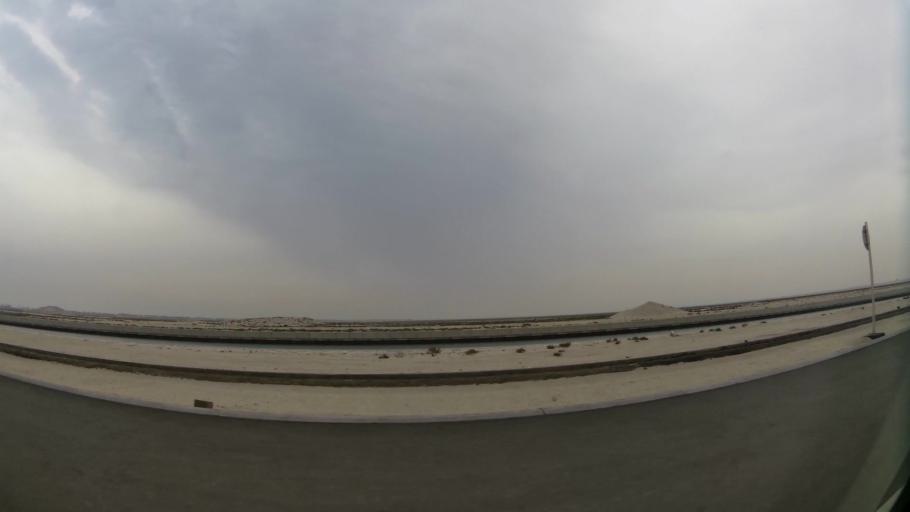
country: BH
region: Central Governorate
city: Dar Kulayb
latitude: 25.8631
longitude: 50.6052
